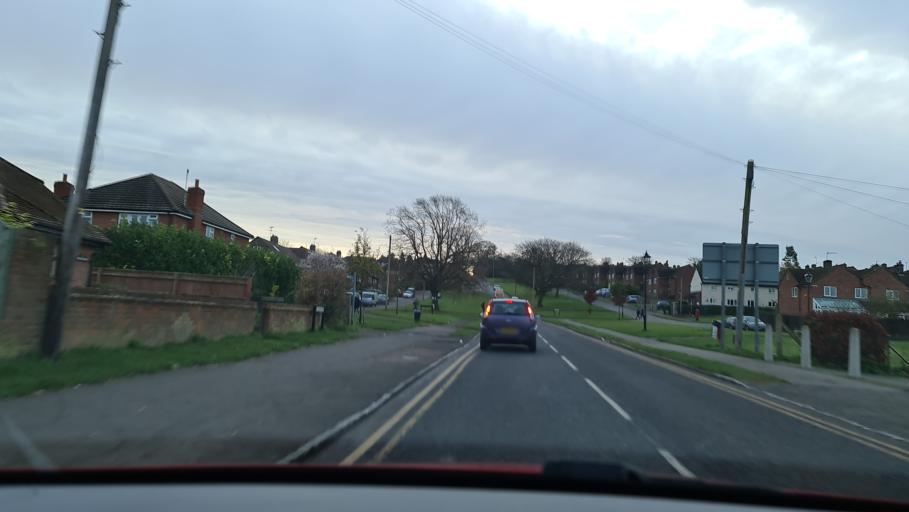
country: GB
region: England
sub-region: Buckinghamshire
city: Princes Risborough
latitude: 51.7231
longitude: -0.8286
